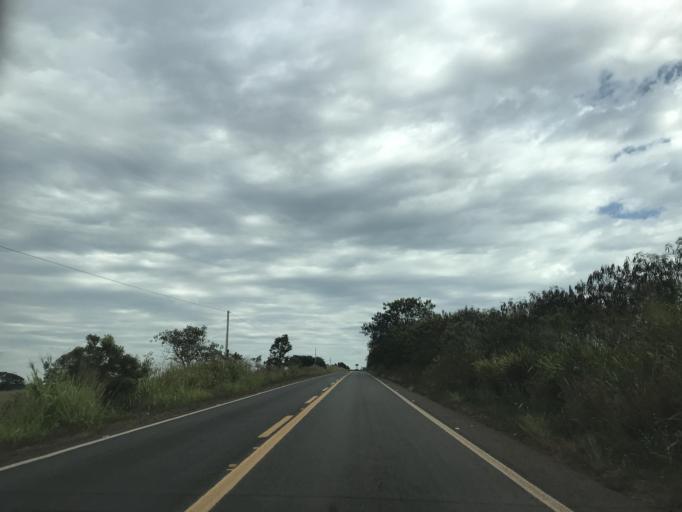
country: BR
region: Goias
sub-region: Piracanjuba
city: Piracanjuba
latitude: -17.1965
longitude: -48.6992
